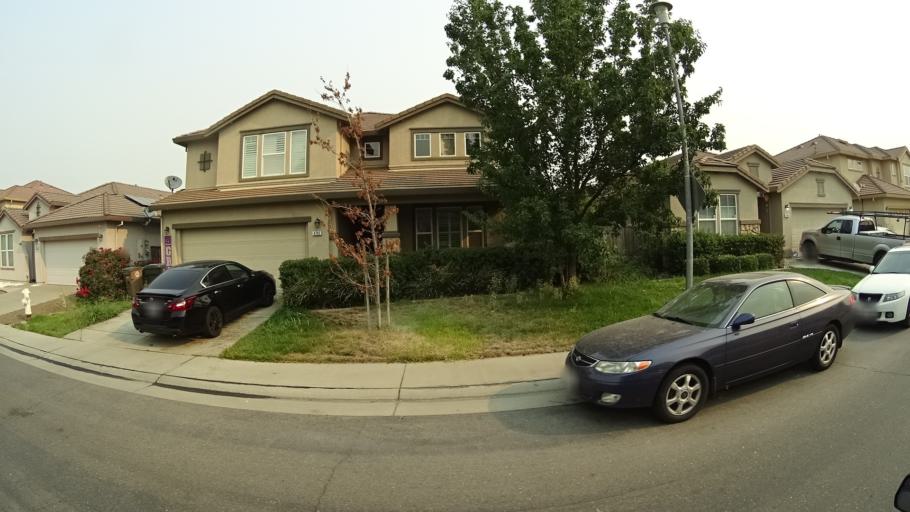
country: US
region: California
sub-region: Sacramento County
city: Laguna
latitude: 38.3993
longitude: -121.4498
